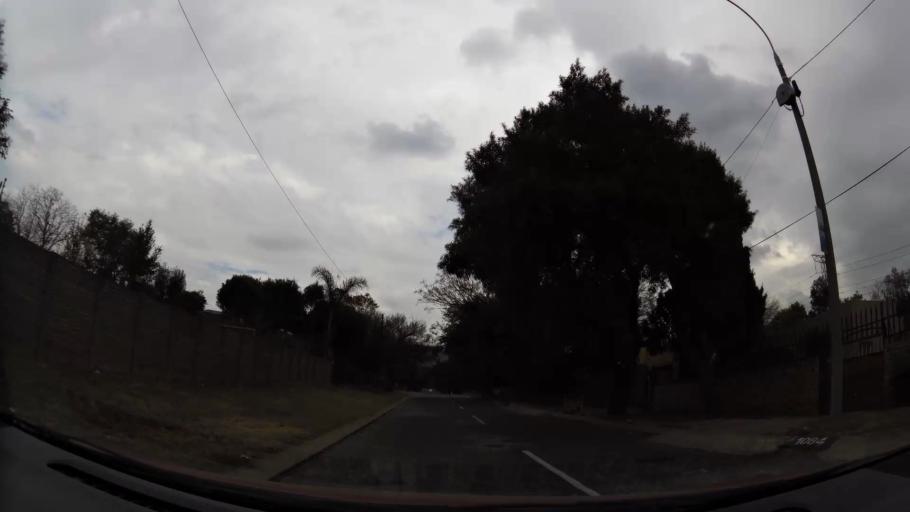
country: ZA
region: Gauteng
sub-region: City of Johannesburg Metropolitan Municipality
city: Roodepoort
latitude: -26.1154
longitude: 27.9009
